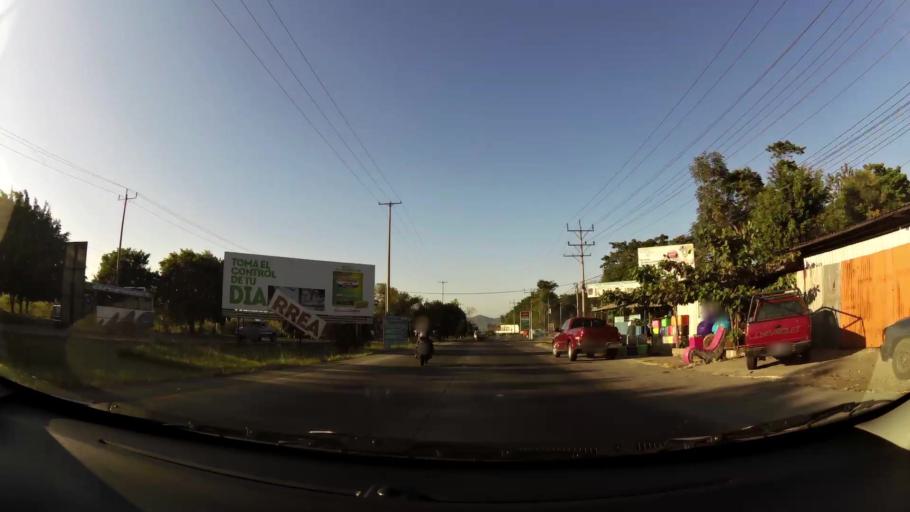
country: SV
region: La Libertad
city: Ciudad Arce
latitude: 13.7560
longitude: -89.3668
